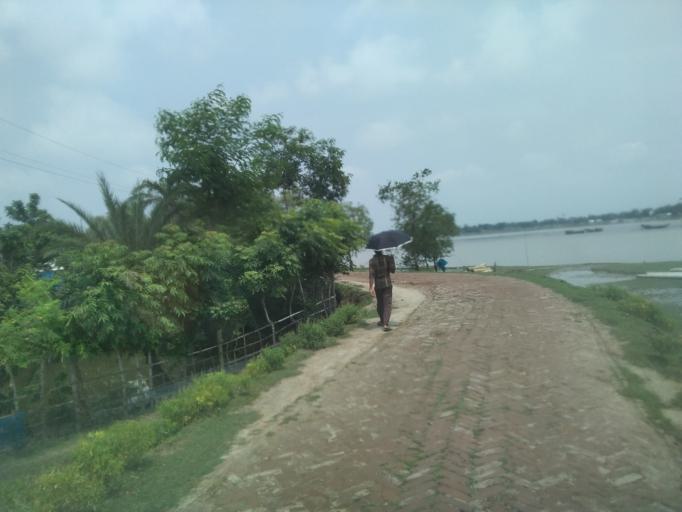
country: BD
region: Khulna
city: Phultala
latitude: 22.6415
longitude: 89.4238
